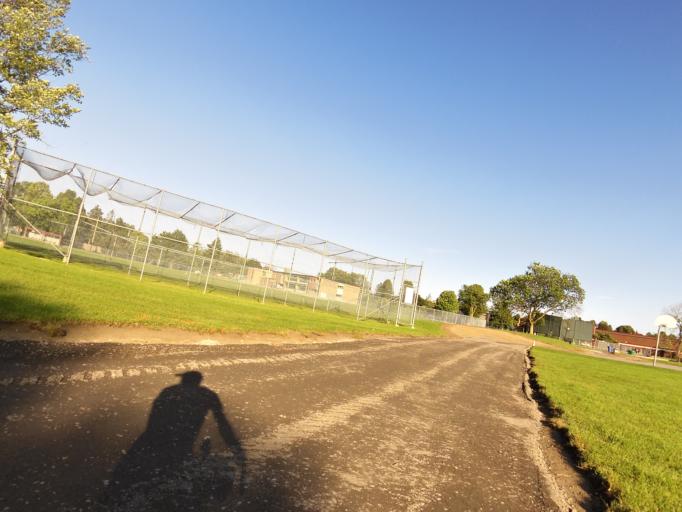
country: CA
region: Ontario
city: Bells Corners
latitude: 45.3496
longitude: -75.7753
